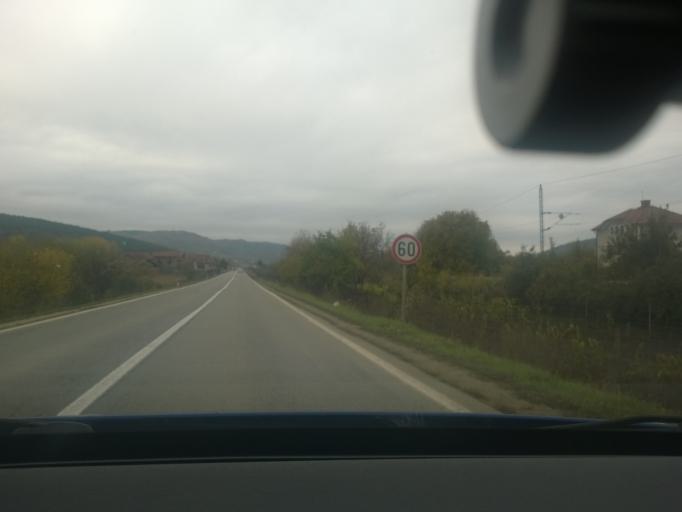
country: RS
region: Central Serbia
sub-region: Pirotski Okrug
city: Dimitrovgrad
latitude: 43.0097
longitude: 22.7578
